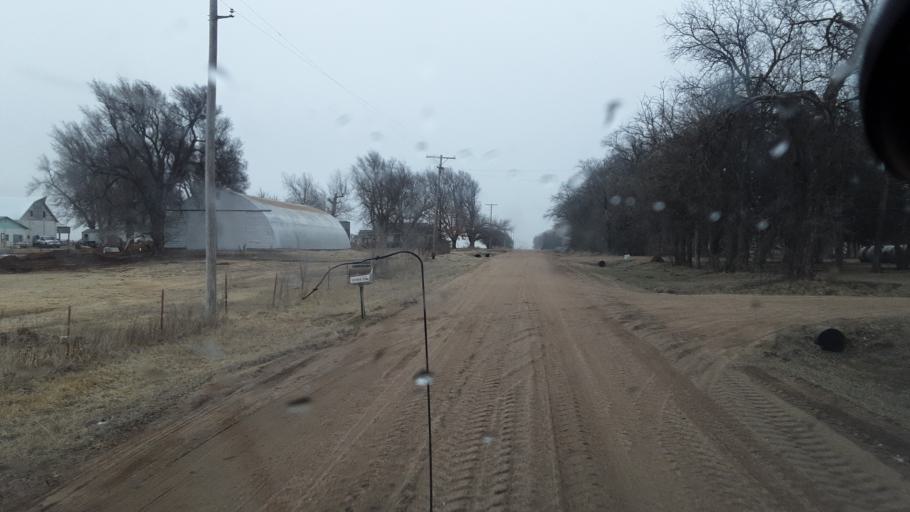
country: US
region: Kansas
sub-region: Reno County
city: South Hutchinson
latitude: 37.9555
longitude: -98.0203
